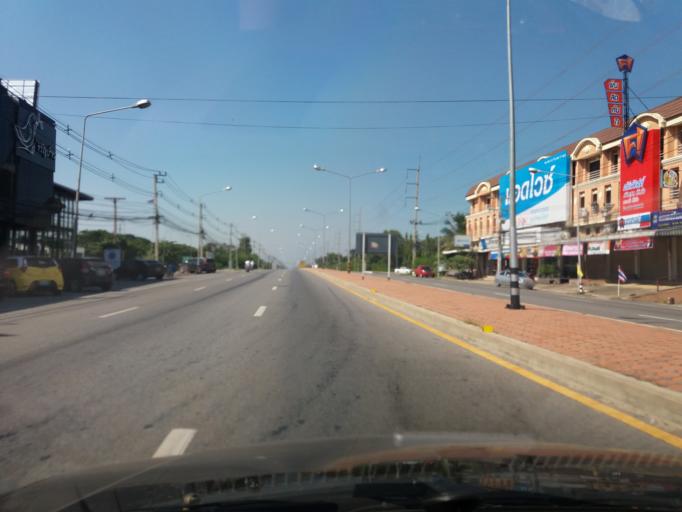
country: TH
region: Chai Nat
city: Chai Nat
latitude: 15.1967
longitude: 100.1256
